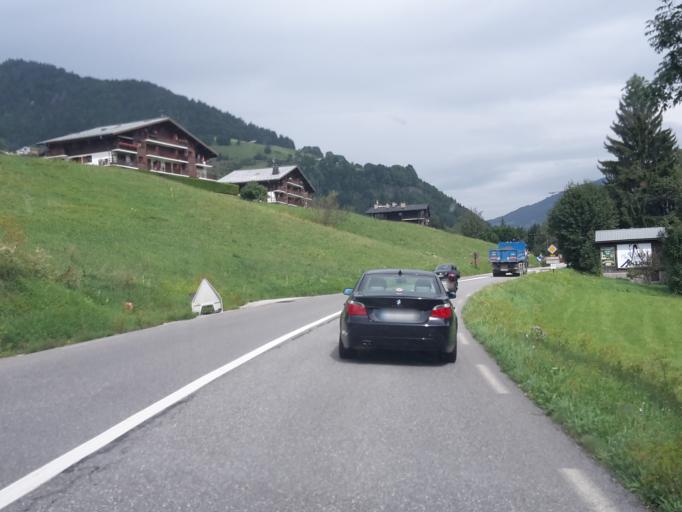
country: FR
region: Rhone-Alpes
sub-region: Departement de la Haute-Savoie
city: Praz-sur-Arly
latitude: 45.8337
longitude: 6.5614
